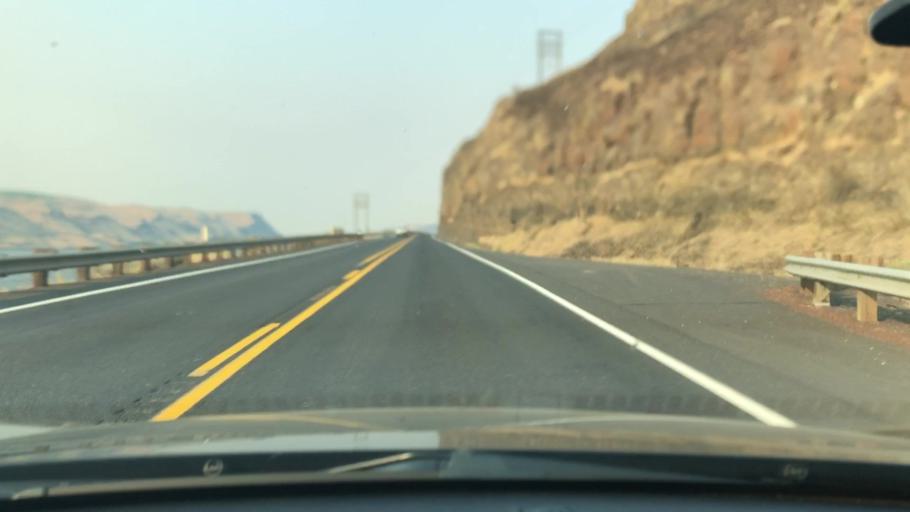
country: US
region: Washington
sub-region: Benton County
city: Highland
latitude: 45.9485
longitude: -119.0635
